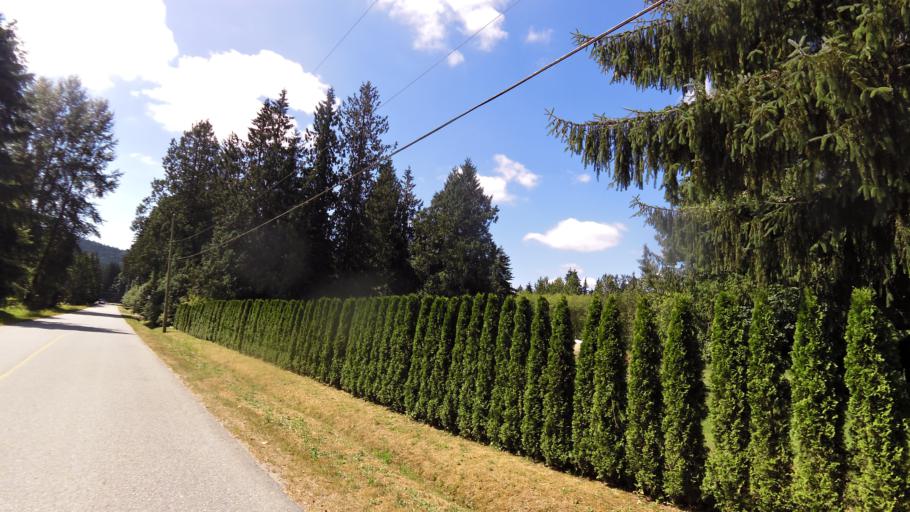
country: CA
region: British Columbia
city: Maple Ridge
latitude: 49.2156
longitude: -122.5266
